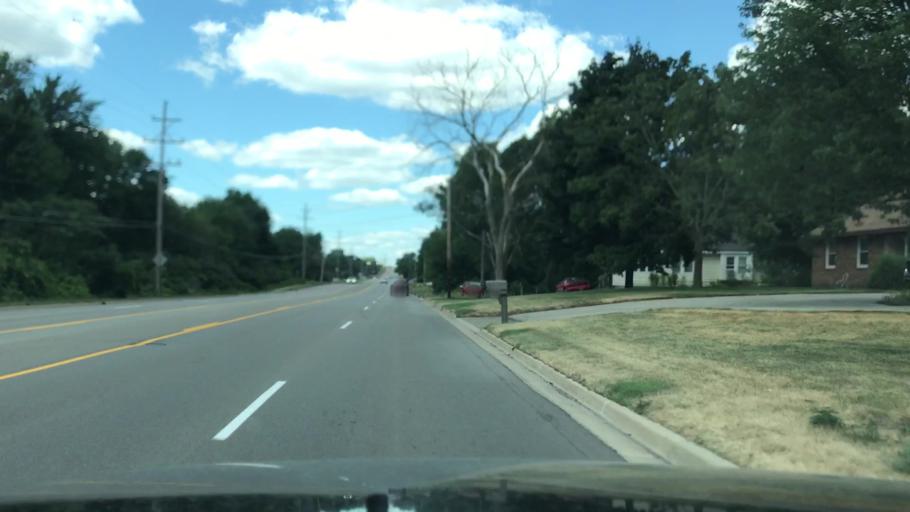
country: US
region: Michigan
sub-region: Kent County
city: Byron Center
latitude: 42.8352
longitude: -85.7230
